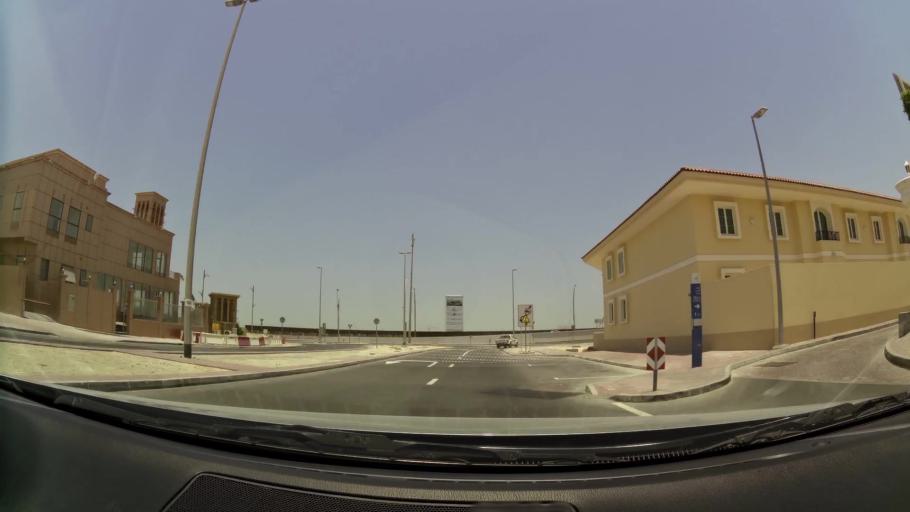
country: AE
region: Dubai
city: Dubai
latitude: 25.1930
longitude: 55.2349
